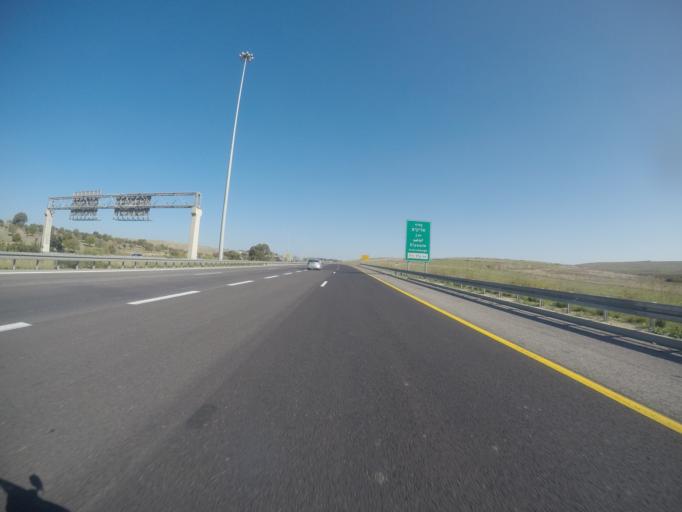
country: IL
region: Haifa
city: Daliyat el Karmil
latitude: 32.6183
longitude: 35.0545
